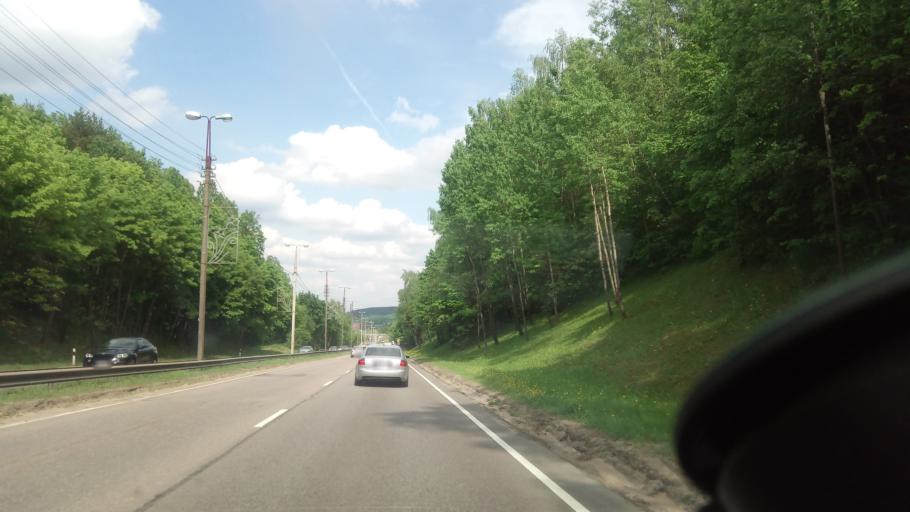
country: LT
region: Vilnius County
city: Lazdynai
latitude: 54.6429
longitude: 25.1947
